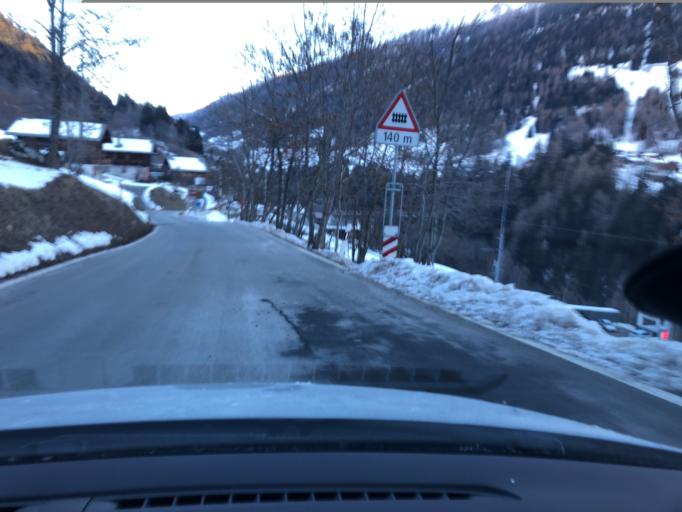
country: CH
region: Valais
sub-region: Goms District
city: Fiesch
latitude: 46.4110
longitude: 8.1502
